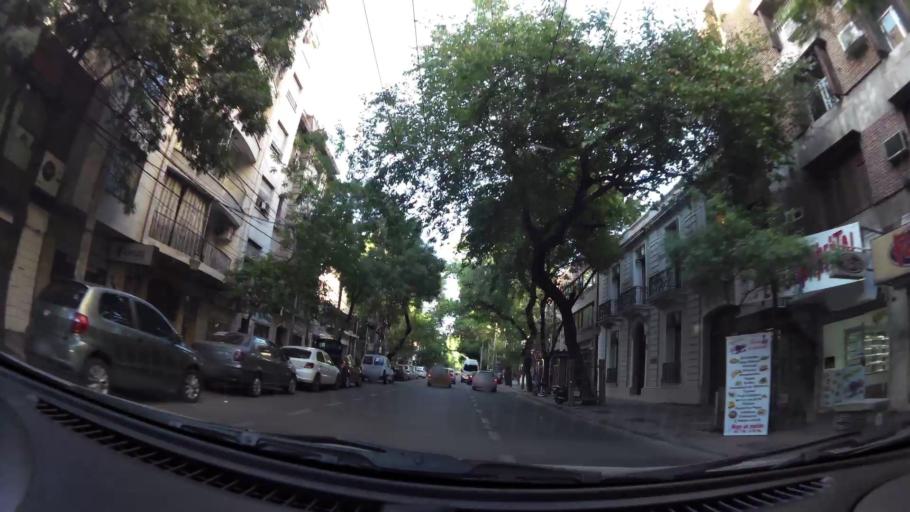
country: AR
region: Mendoza
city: Mendoza
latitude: -32.8919
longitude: -68.8412
